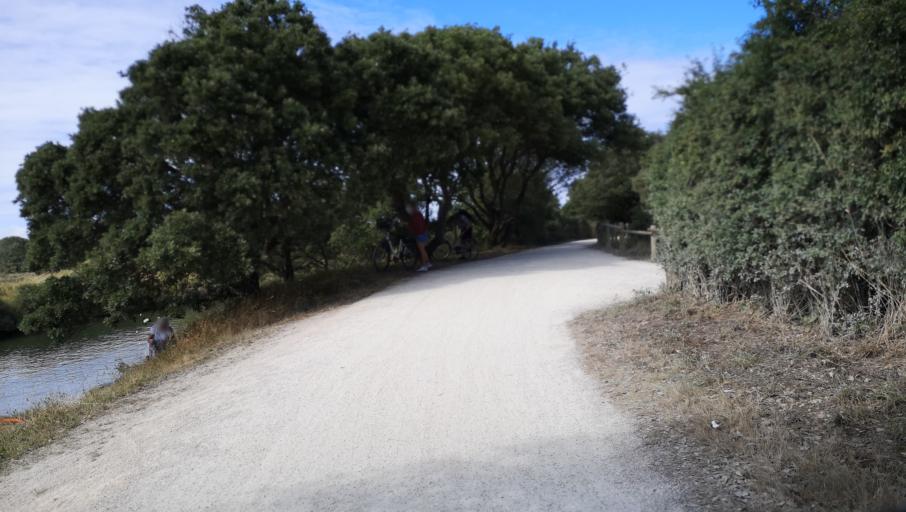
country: FR
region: Pays de la Loire
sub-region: Departement de la Vendee
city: Olonne-sur-Mer
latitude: 46.5300
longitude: -1.8089
